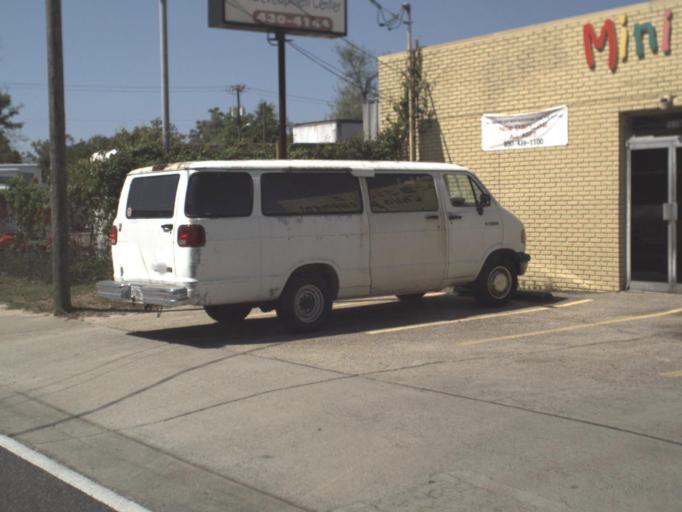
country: US
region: Florida
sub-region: Escambia County
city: Pensacola
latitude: 30.4243
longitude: -87.2411
